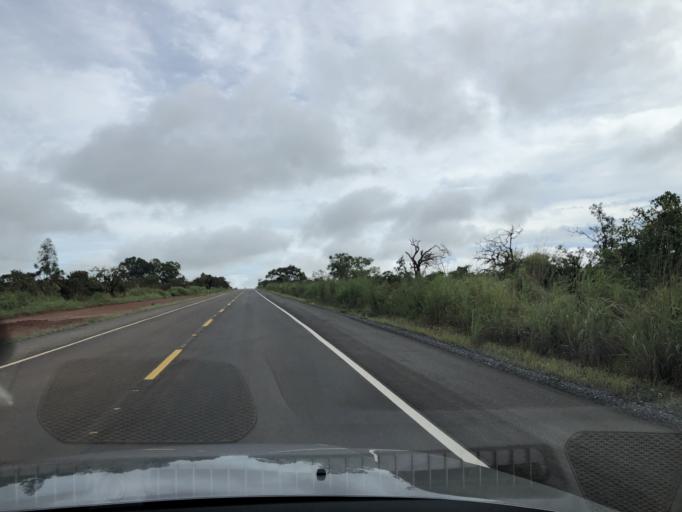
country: BR
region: Federal District
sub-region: Brasilia
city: Brasilia
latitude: -15.6399
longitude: -48.0788
